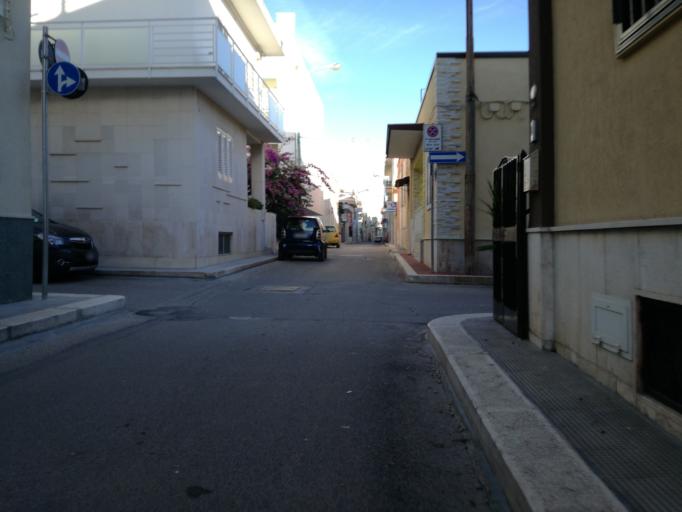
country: IT
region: Apulia
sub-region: Provincia di Bari
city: Adelfia
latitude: 41.0013
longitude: 16.8657
